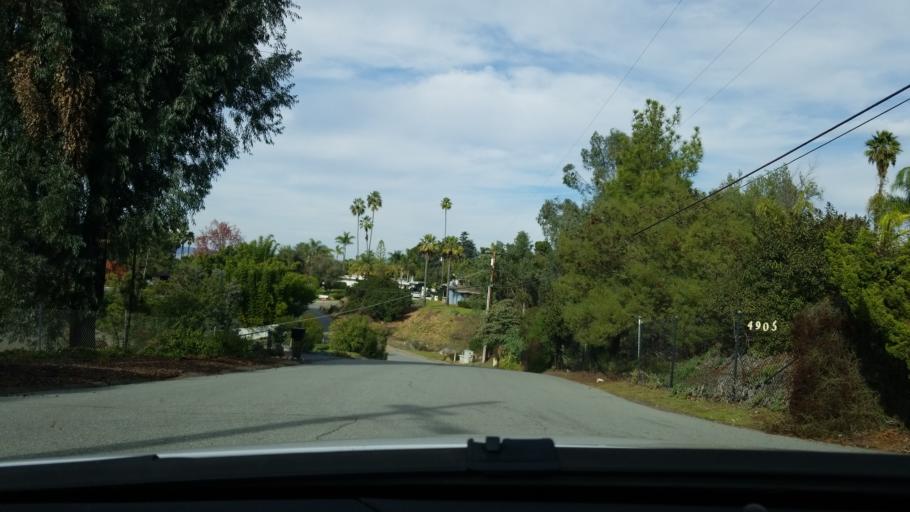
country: US
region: California
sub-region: San Diego County
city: Casa de Oro-Mount Helix
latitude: 32.7700
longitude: -116.9536
